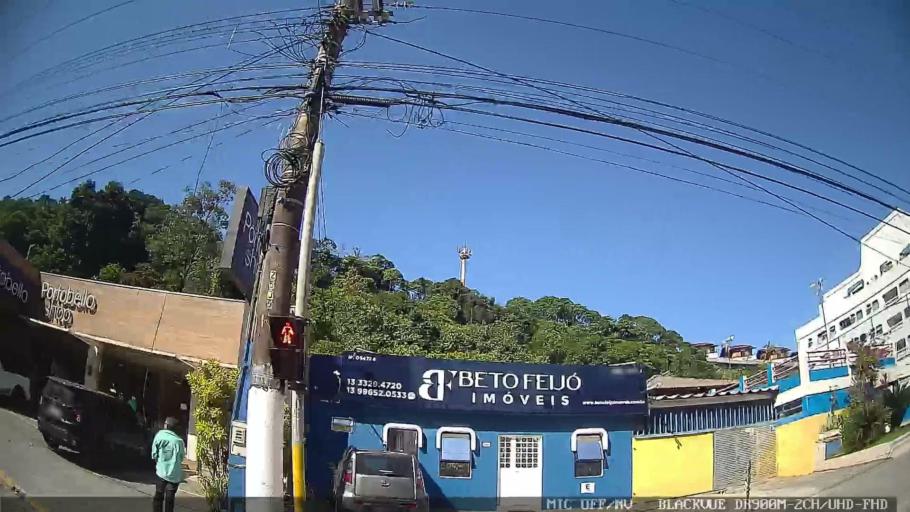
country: BR
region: Sao Paulo
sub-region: Guaruja
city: Guaruja
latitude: -23.9860
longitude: -46.2405
